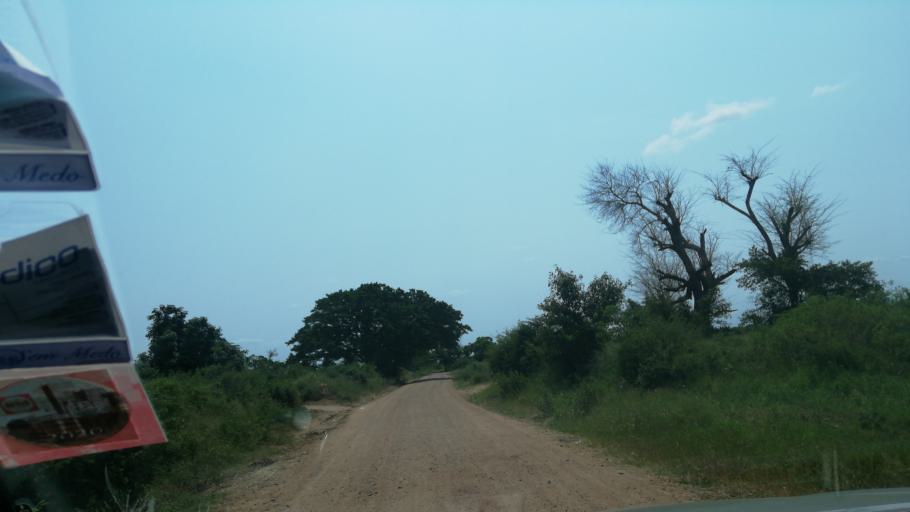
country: MZ
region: Maputo
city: Matola
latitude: -26.0586
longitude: 32.3896
